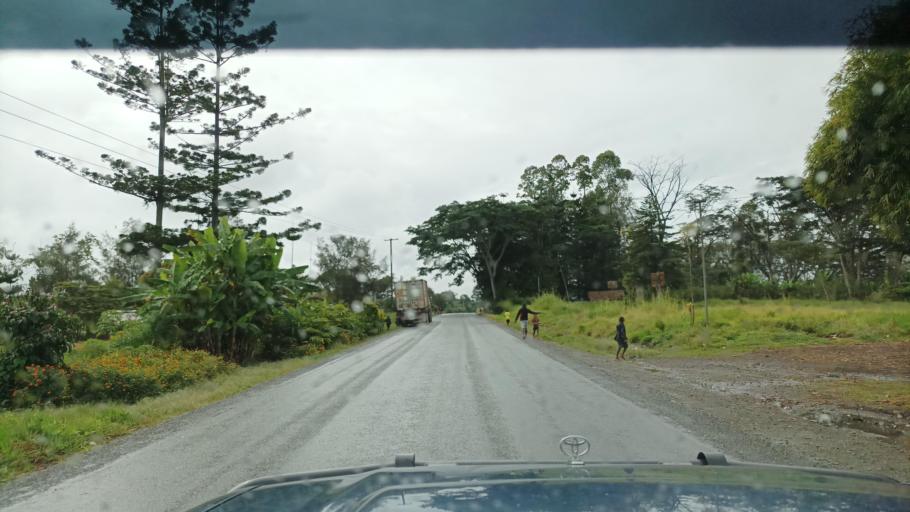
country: PG
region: Jiwaka
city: Minj
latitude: -5.8736
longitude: 144.6614
